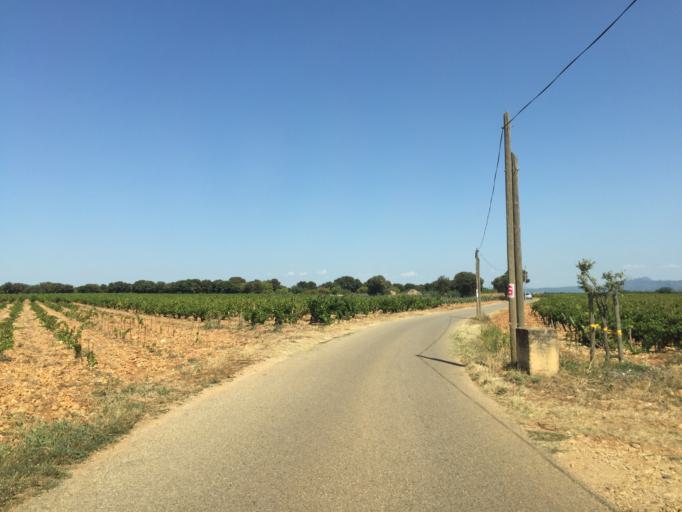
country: FR
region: Provence-Alpes-Cote d'Azur
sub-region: Departement du Vaucluse
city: Courthezon
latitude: 44.1041
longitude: 4.8455
